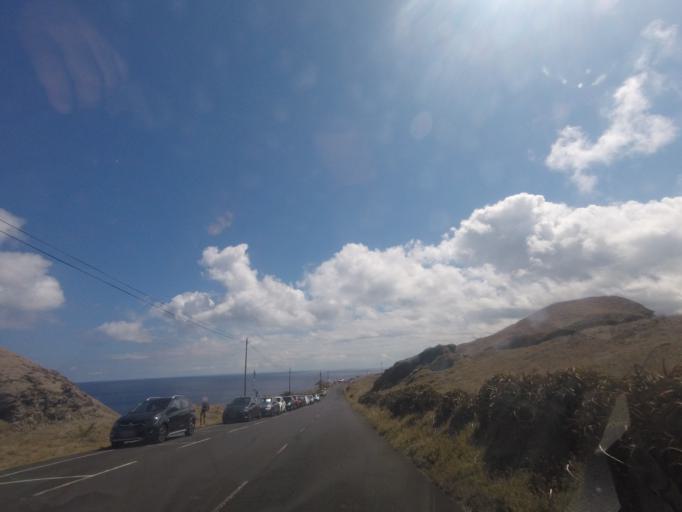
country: PT
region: Madeira
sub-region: Machico
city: Canical
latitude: 32.7456
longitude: -16.7156
